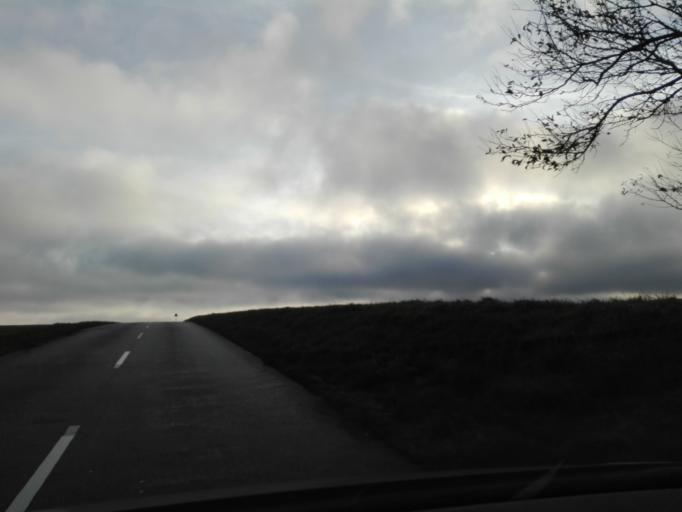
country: DK
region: Central Jutland
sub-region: Arhus Kommune
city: Solbjerg
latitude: 56.0237
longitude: 10.1068
